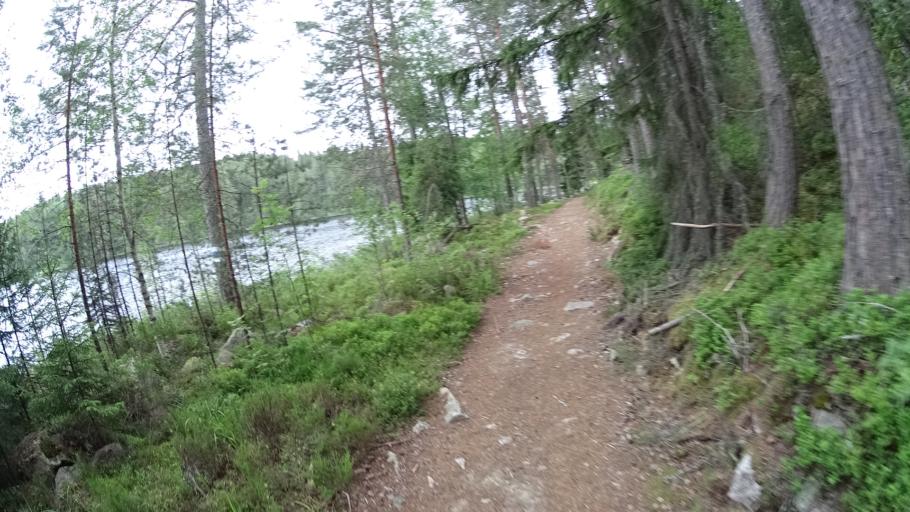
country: FI
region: Southern Savonia
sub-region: Mikkeli
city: Maentyharju
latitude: 61.1795
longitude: 26.8980
